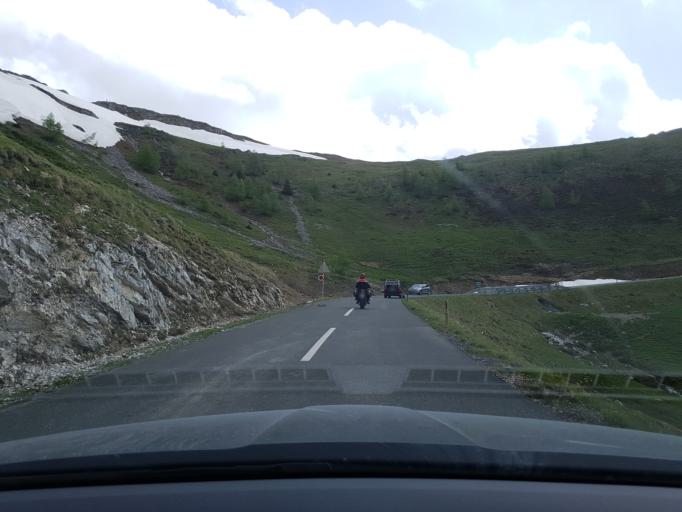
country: AT
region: Carinthia
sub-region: Politischer Bezirk Spittal an der Drau
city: Kleinkirchheim
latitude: 46.9389
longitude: 13.7571
